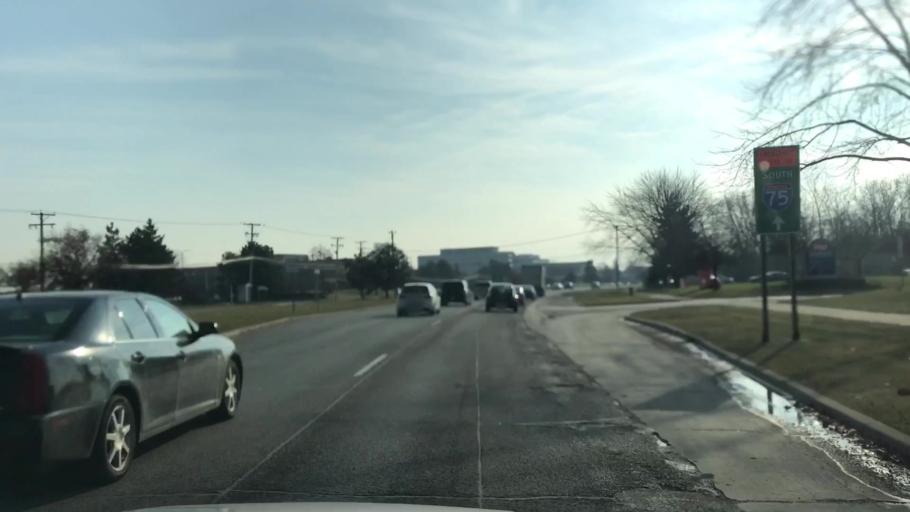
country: US
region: Michigan
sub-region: Oakland County
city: Clawson
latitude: 42.5482
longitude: -83.1215
